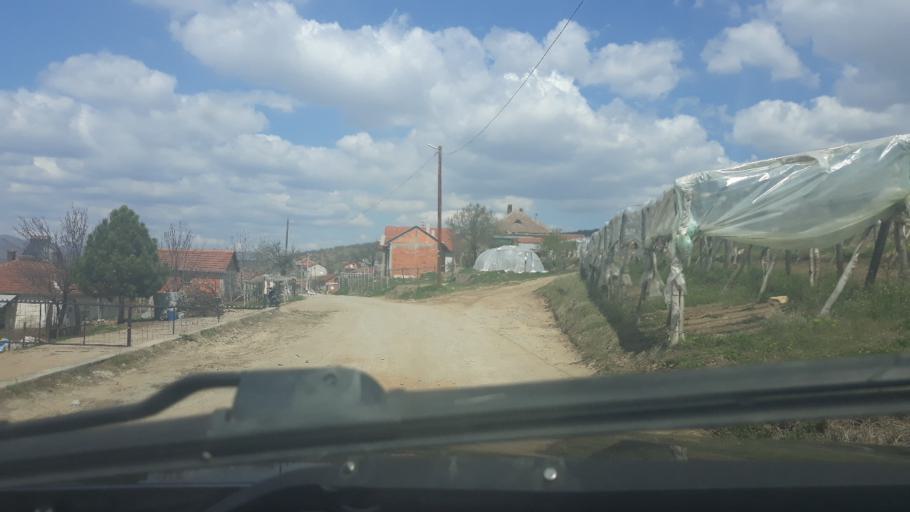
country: MK
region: Caska
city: Caska
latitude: 41.6483
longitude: 21.6935
